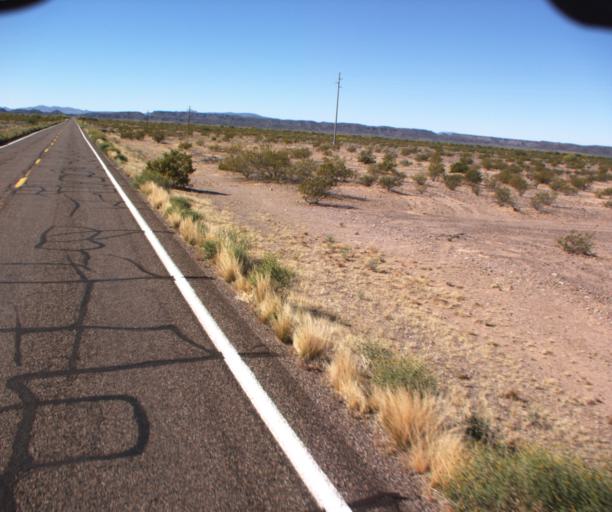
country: US
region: Arizona
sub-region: Pima County
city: Ajo
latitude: 32.6267
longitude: -112.8656
